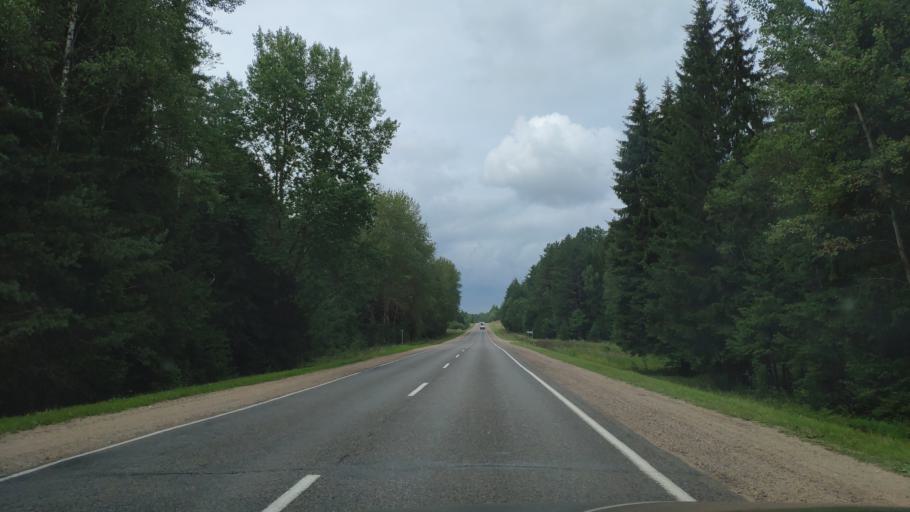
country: BY
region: Minsk
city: Novosel'ye
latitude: 53.9560
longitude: 27.2455
